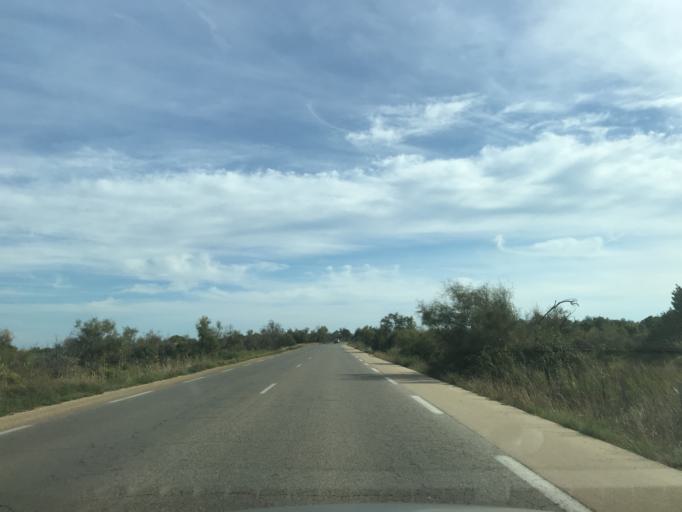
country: FR
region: Provence-Alpes-Cote d'Azur
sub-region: Departement des Bouches-du-Rhone
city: Saintes-Maries-de-la-Mer
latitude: 43.4947
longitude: 4.4032
